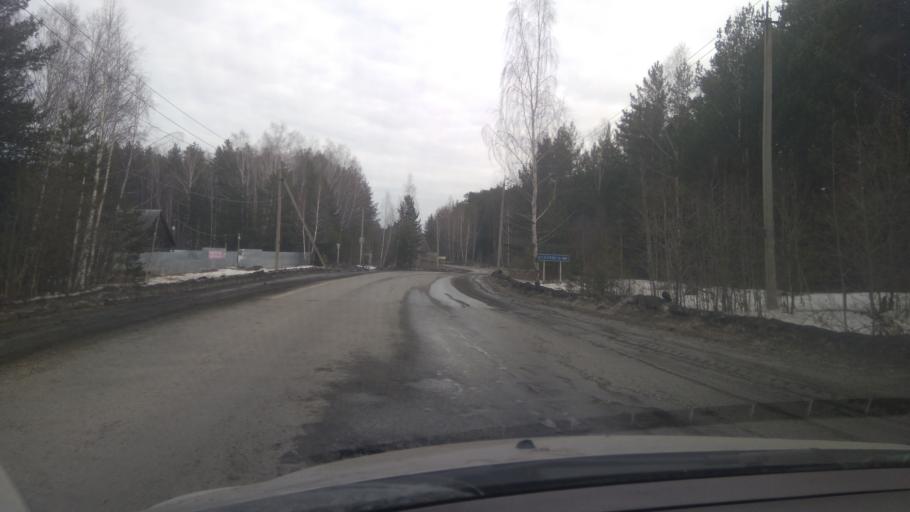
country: RU
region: Sverdlovsk
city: Severka
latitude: 56.8332
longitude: 60.3899
